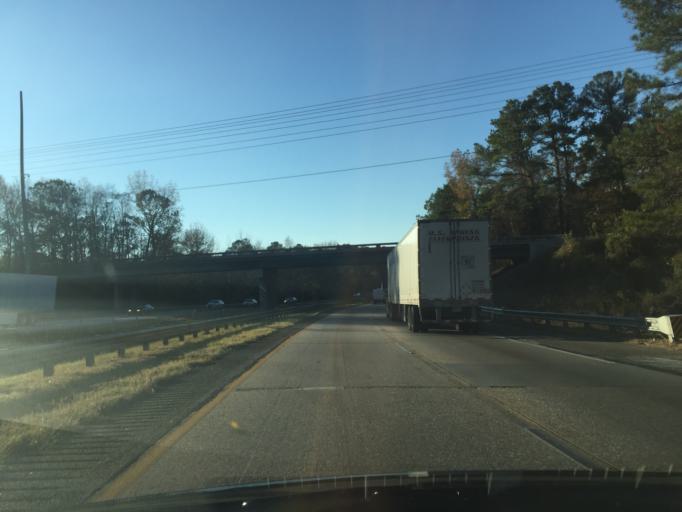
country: US
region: Georgia
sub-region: Bibb County
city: West Point
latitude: 32.9401
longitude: -83.7805
